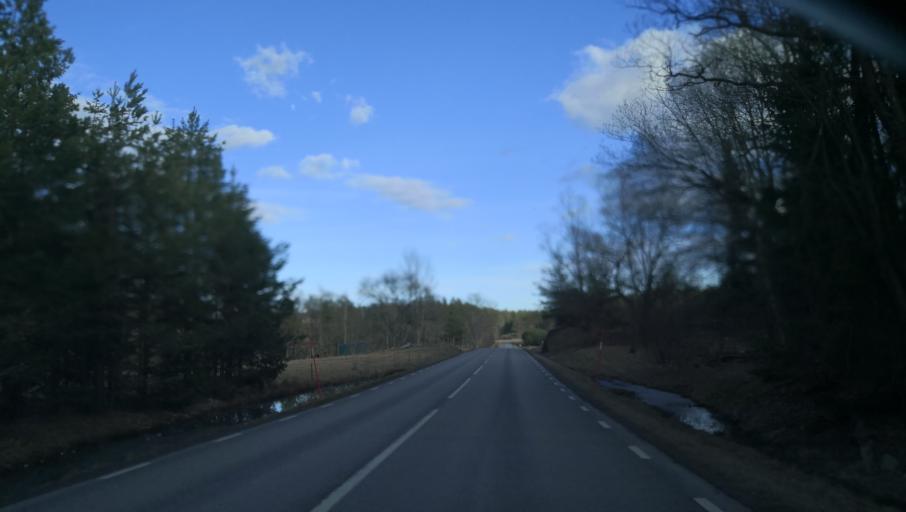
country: SE
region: Stockholm
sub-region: Varmdo Kommun
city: Gustavsberg
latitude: 59.3485
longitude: 18.3758
